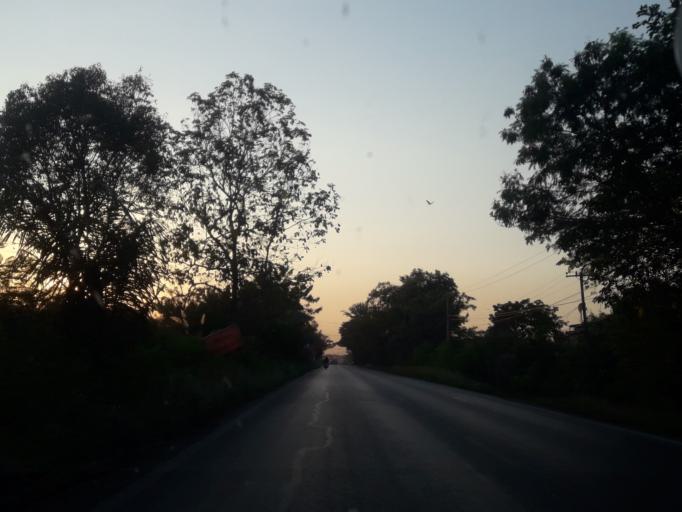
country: TH
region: Pathum Thani
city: Nong Suea
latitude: 14.1315
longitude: 100.7697
